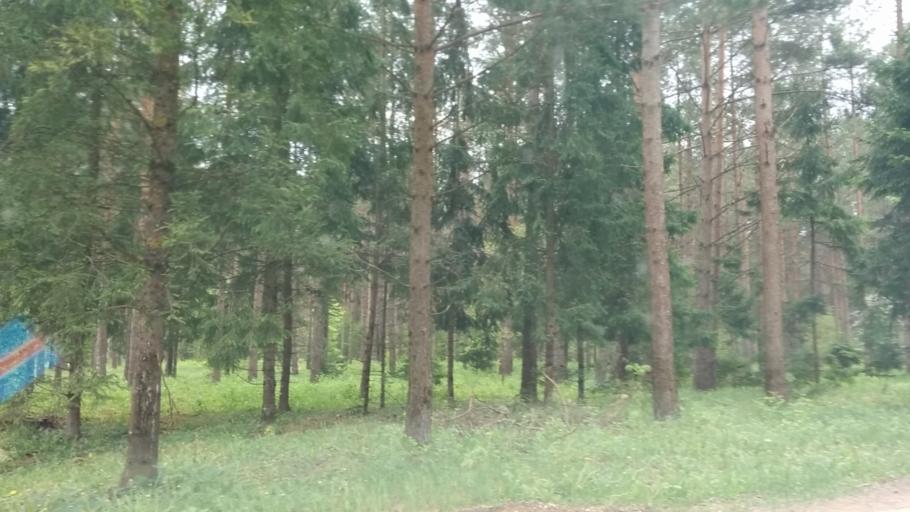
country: LV
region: Babite
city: Pinki
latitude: 56.9331
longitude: 23.9344
